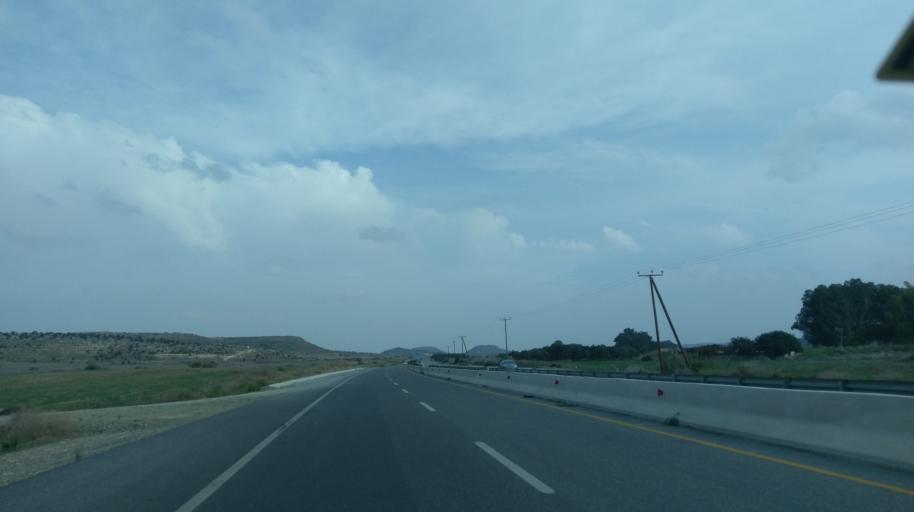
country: CY
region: Lefkosia
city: Peristerona
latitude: 35.1960
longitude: 33.0934
